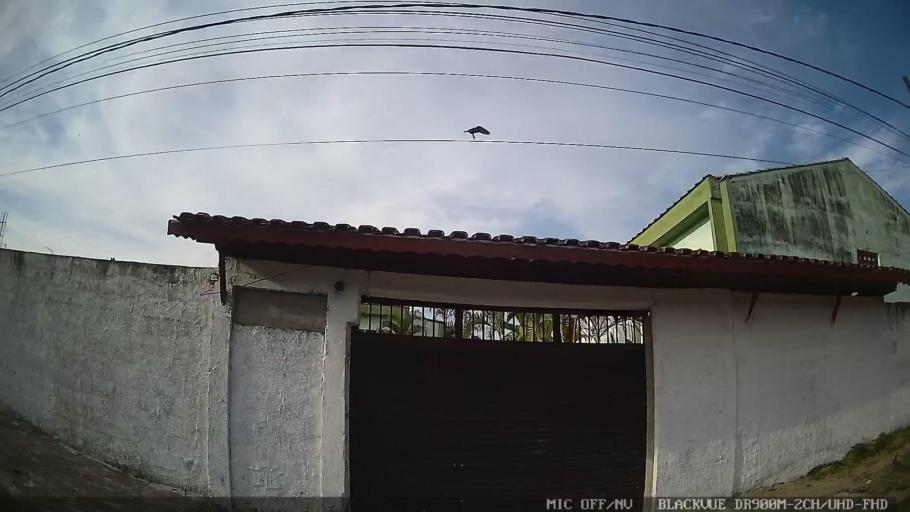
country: BR
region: Sao Paulo
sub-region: Itanhaem
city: Itanhaem
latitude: -24.1657
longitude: -46.7674
